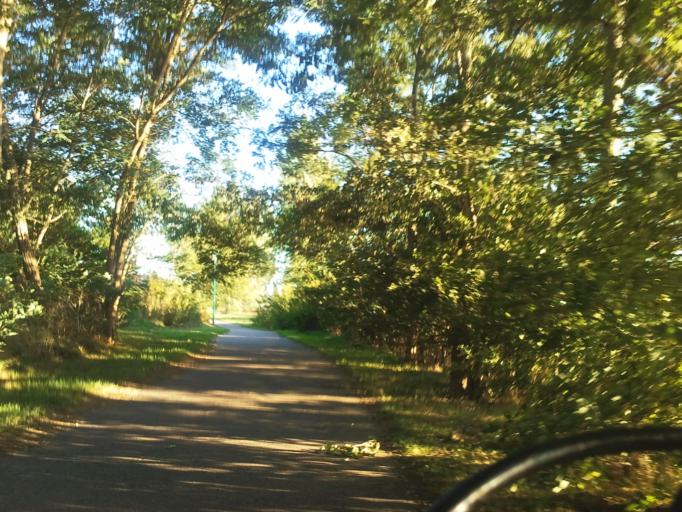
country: DE
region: Mecklenburg-Vorpommern
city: Rostock
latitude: 54.1165
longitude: 12.0989
